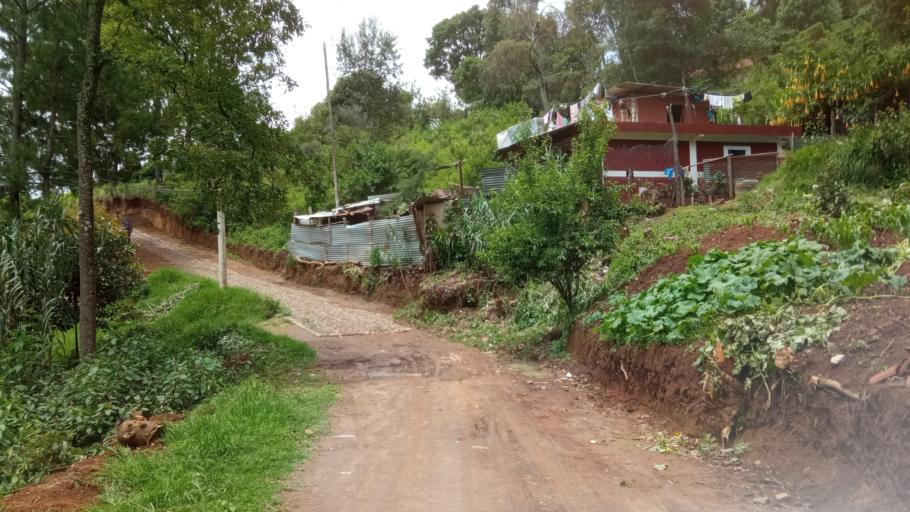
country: GT
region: San Marcos
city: Tejutla
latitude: 15.1163
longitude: -91.8063
